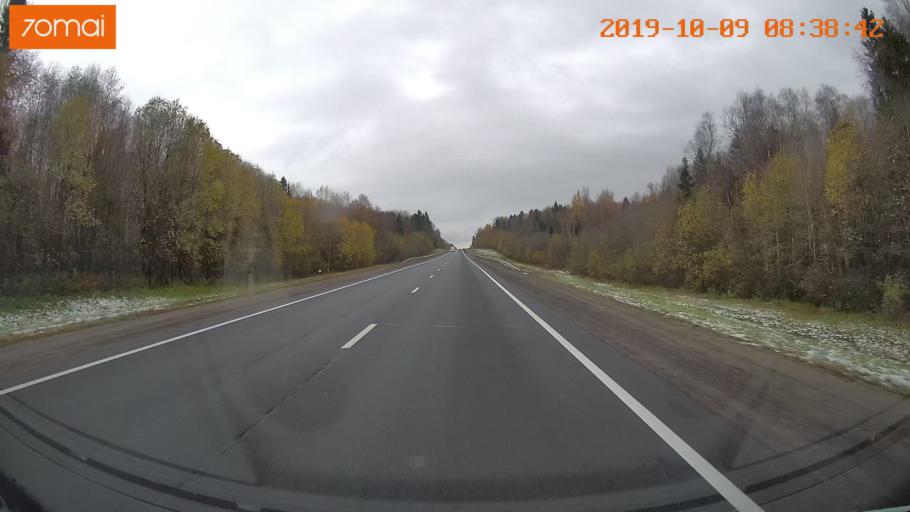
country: RU
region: Vologda
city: Gryazovets
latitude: 58.9605
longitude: 40.1624
